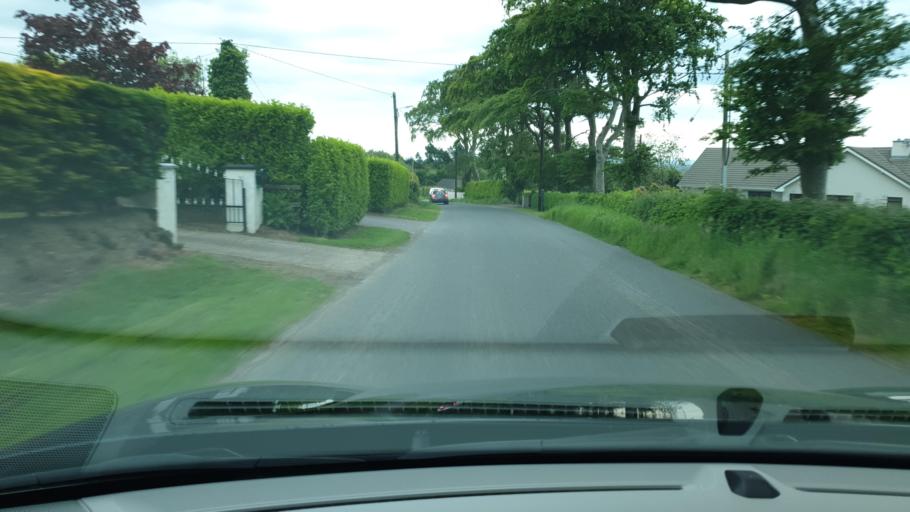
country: IE
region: Leinster
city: Balrothery
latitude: 53.5605
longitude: -6.1793
